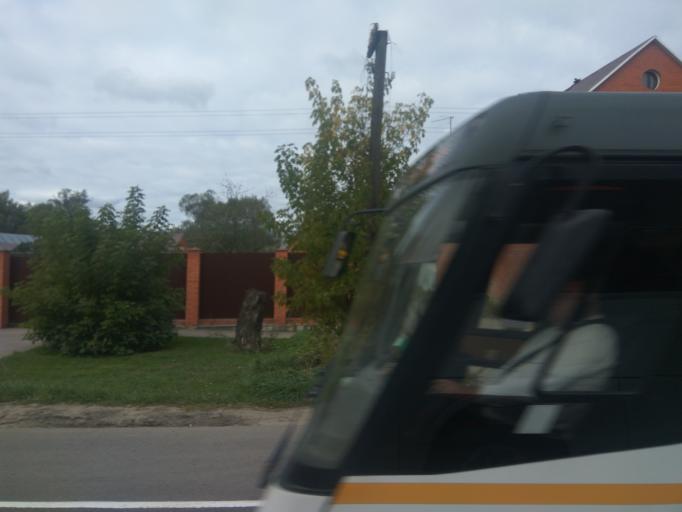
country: RU
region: Moskovskaya
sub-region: Shchelkovskiy Rayon
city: Grebnevo
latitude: 55.9887
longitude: 38.1260
